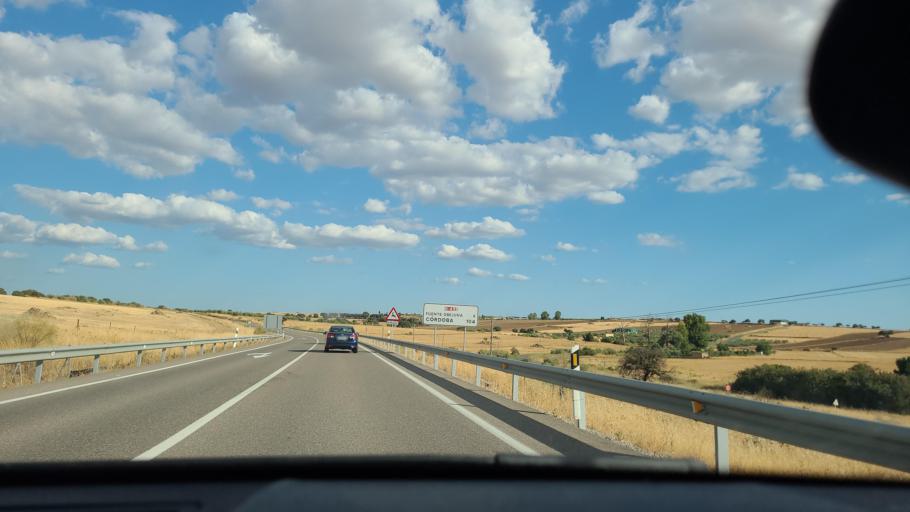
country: ES
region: Andalusia
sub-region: Province of Cordoba
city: Fuente Obejuna
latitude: 38.2676
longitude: -5.5040
